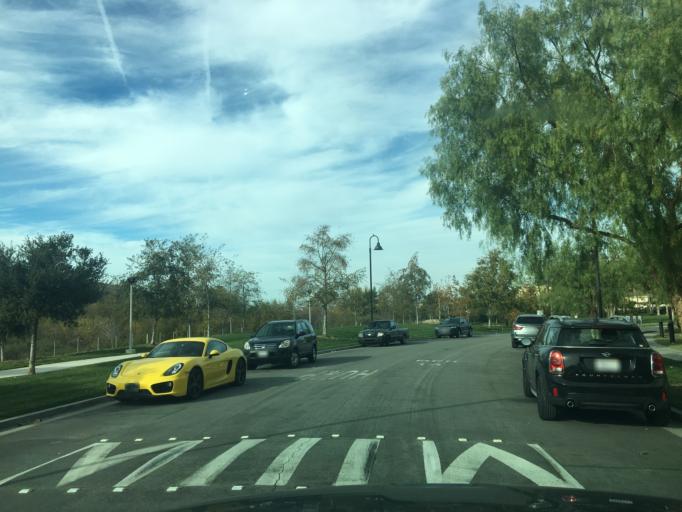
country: US
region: California
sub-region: Orange County
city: Laguna Woods
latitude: 33.6455
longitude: -117.7530
